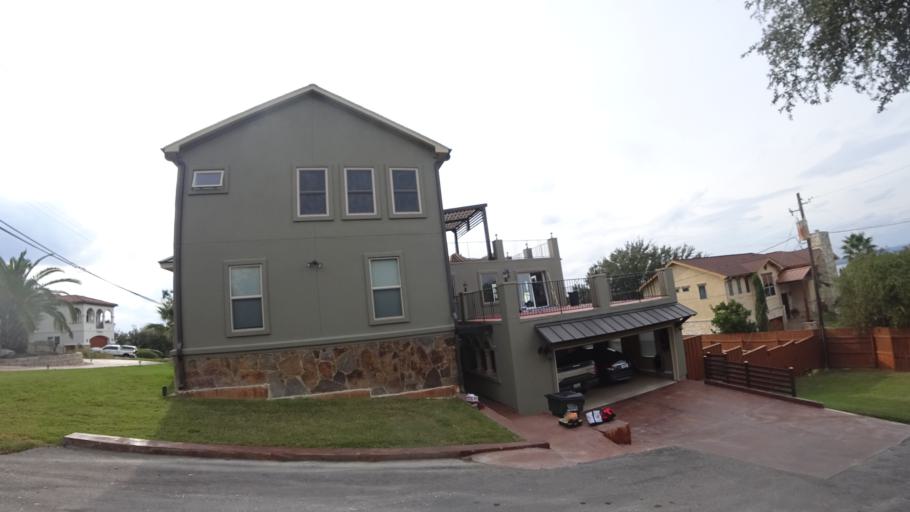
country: US
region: Texas
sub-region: Travis County
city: Hudson Bend
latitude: 30.3940
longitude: -97.8841
